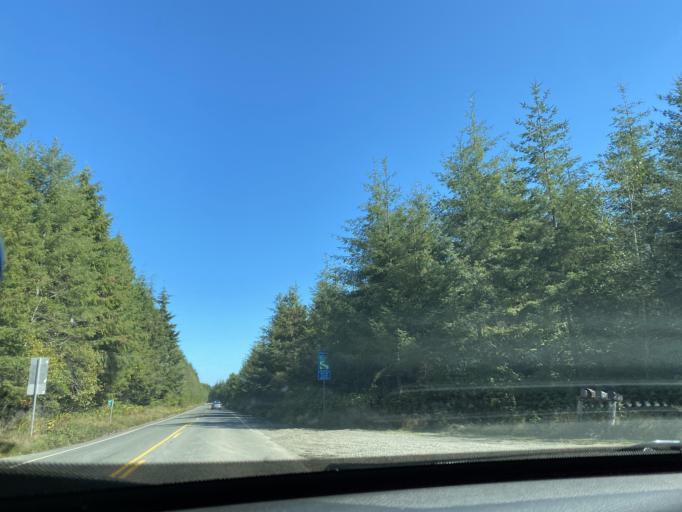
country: US
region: Washington
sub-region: Clallam County
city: Forks
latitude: 47.9308
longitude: -124.4819
